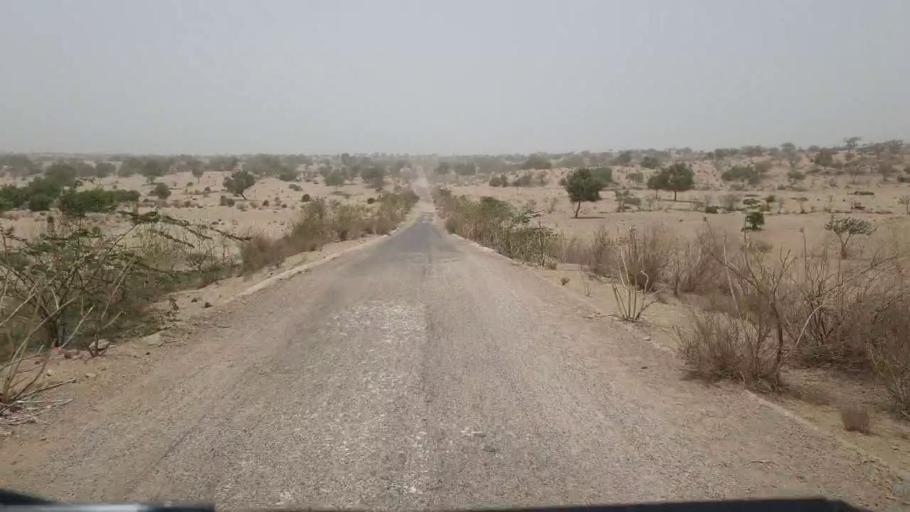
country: PK
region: Sindh
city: Naukot
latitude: 24.7635
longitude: 69.5446
